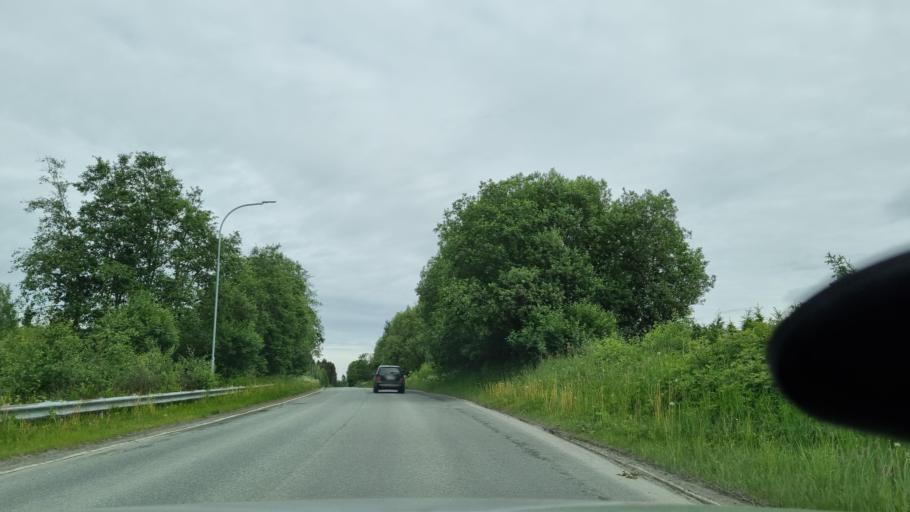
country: NO
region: Sor-Trondelag
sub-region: Melhus
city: Melhus
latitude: 63.3548
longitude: 10.3372
